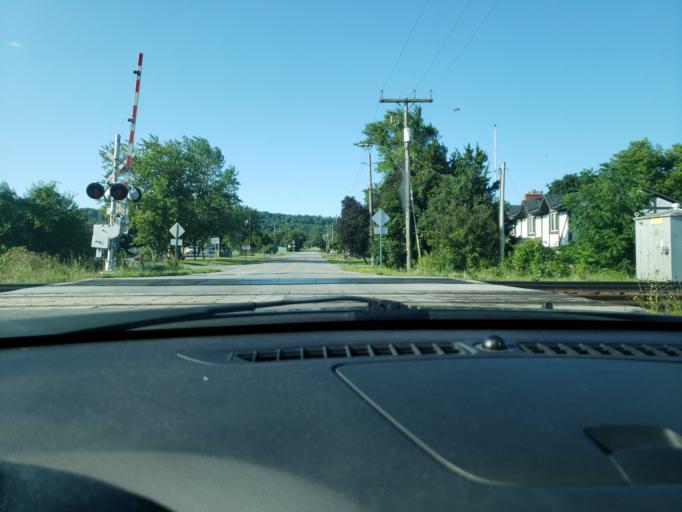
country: CA
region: Ontario
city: Hamilton
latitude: 43.2074
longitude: -79.6143
